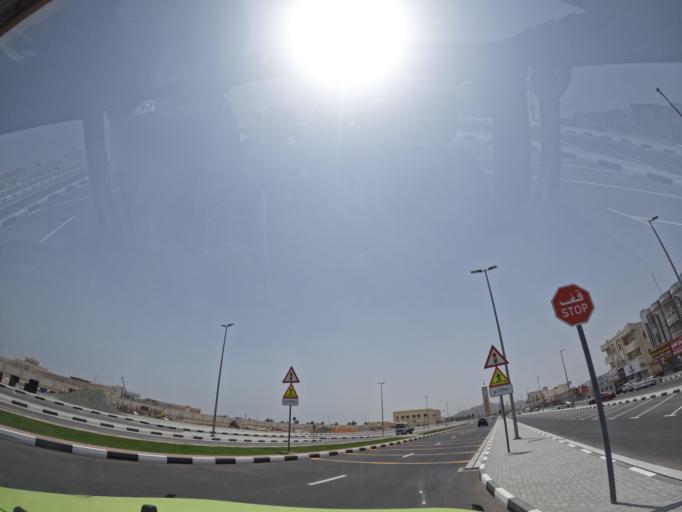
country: AE
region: Al Fujayrah
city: Al Fujayrah
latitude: 25.0222
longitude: 56.3515
